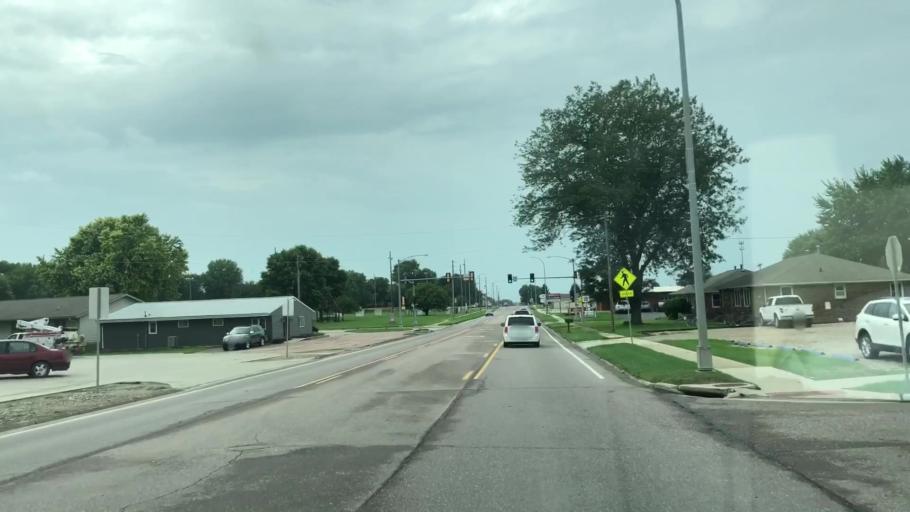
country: US
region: Iowa
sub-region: O'Brien County
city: Sheldon
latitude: 43.1860
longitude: -95.8472
